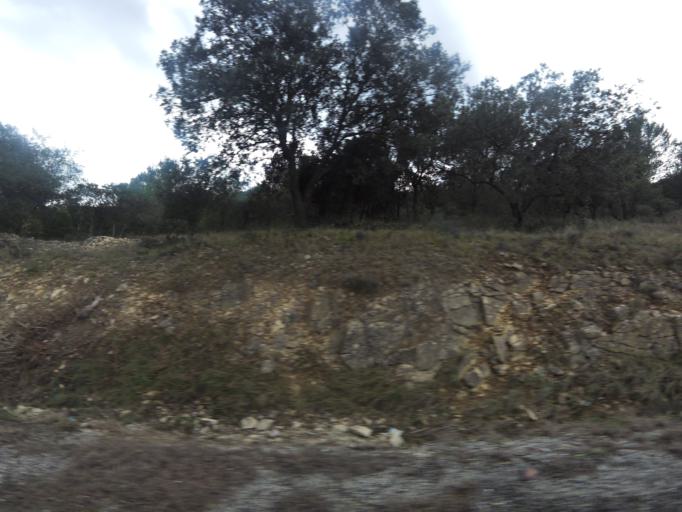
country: FR
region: Languedoc-Roussillon
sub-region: Departement du Gard
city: Saint-Mamert-du-Gard
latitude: 43.8618
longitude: 4.2082
